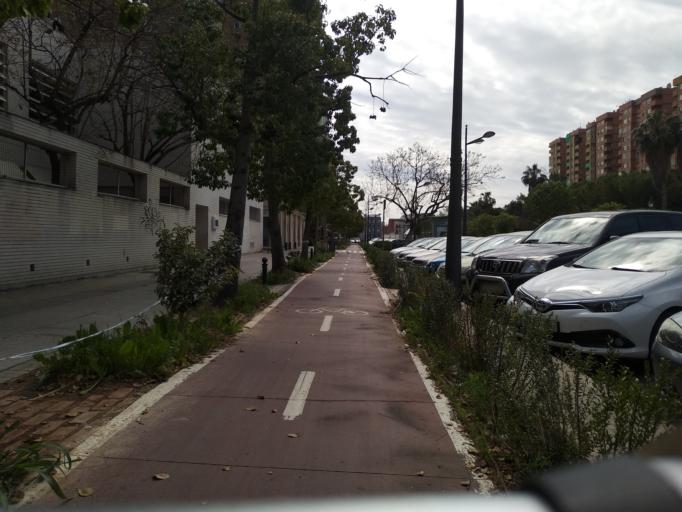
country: ES
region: Valencia
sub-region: Provincia de Valencia
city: Alboraya
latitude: 39.4713
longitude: -0.3376
